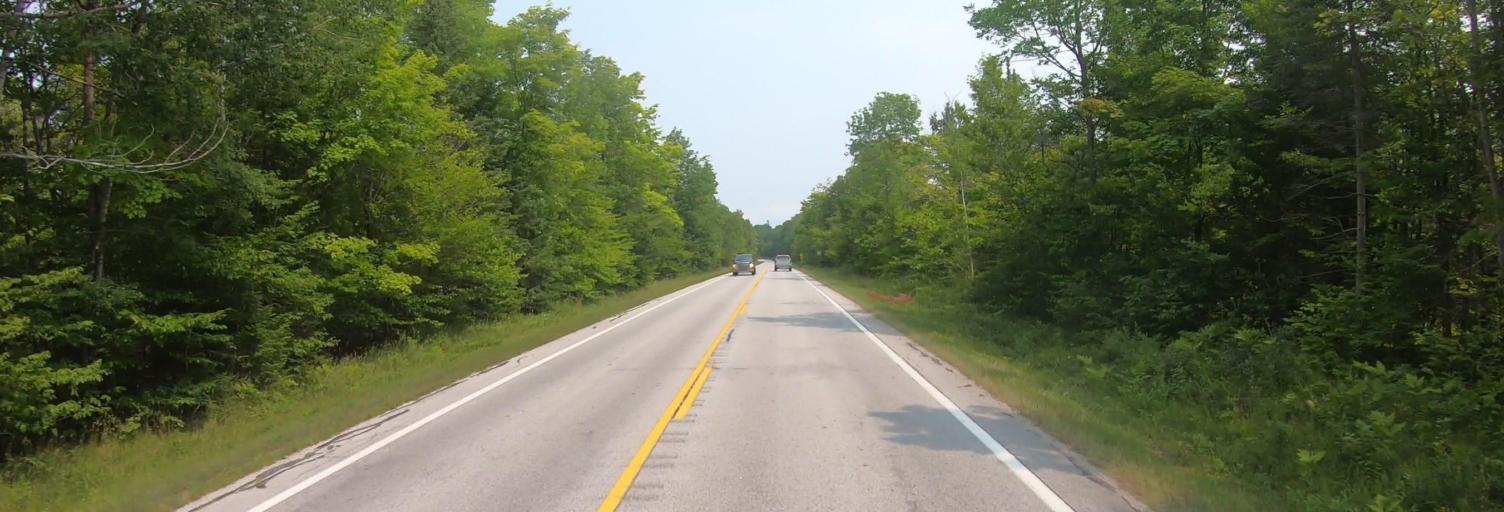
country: CA
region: Ontario
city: Thessalon
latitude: 45.9863
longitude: -83.7843
